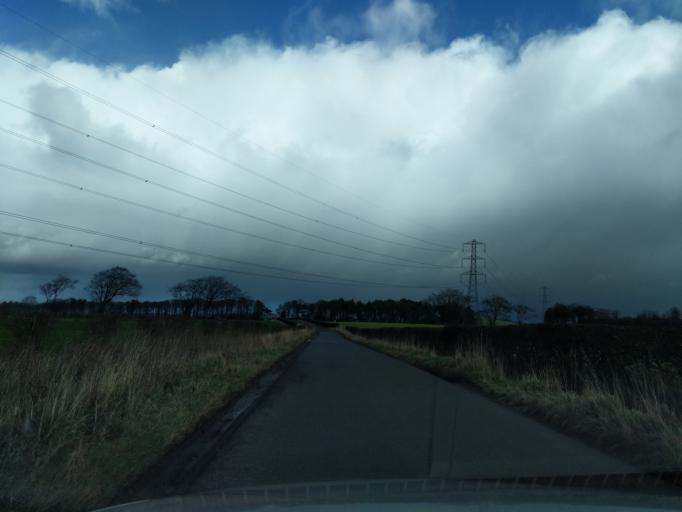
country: GB
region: Scotland
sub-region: Edinburgh
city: Currie
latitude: 55.8785
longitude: -3.3119
